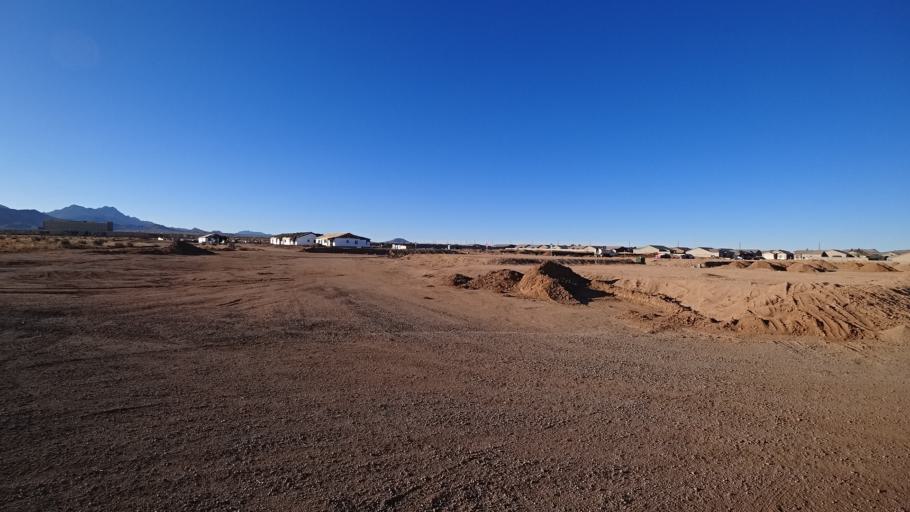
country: US
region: Arizona
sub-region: Mohave County
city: New Kingman-Butler
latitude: 35.2244
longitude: -113.9888
